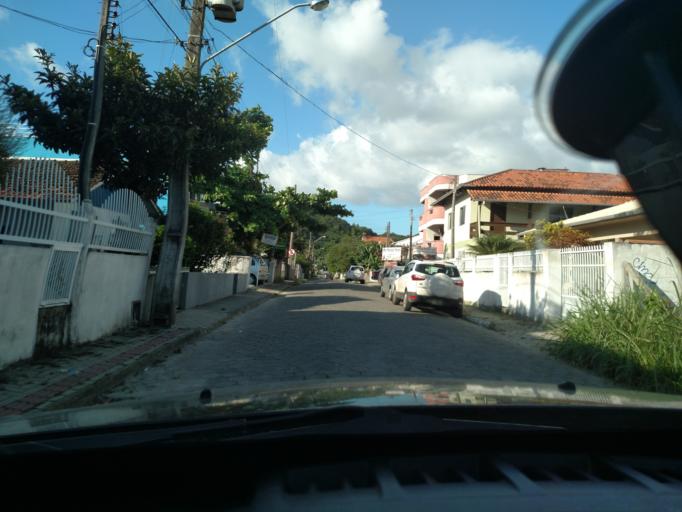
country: BR
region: Santa Catarina
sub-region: Porto Belo
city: Porto Belo
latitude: -27.1536
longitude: -48.4876
